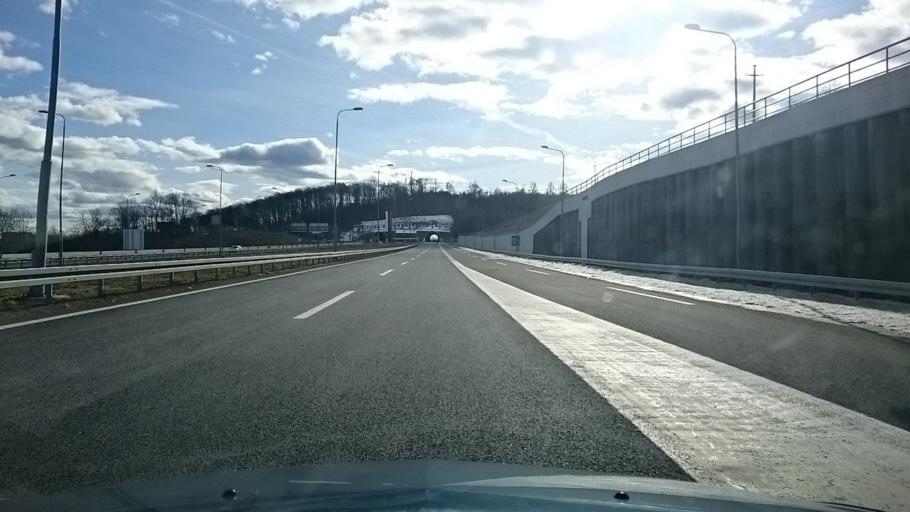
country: BA
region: Republika Srpska
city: Laktasi
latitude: 44.9143
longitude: 17.2964
